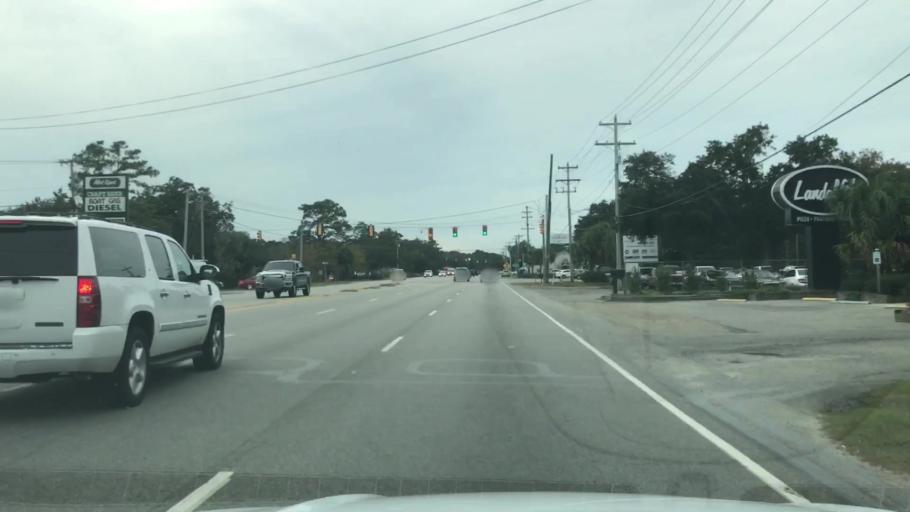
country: US
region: South Carolina
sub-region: Georgetown County
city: Georgetown
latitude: 33.4305
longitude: -79.1451
